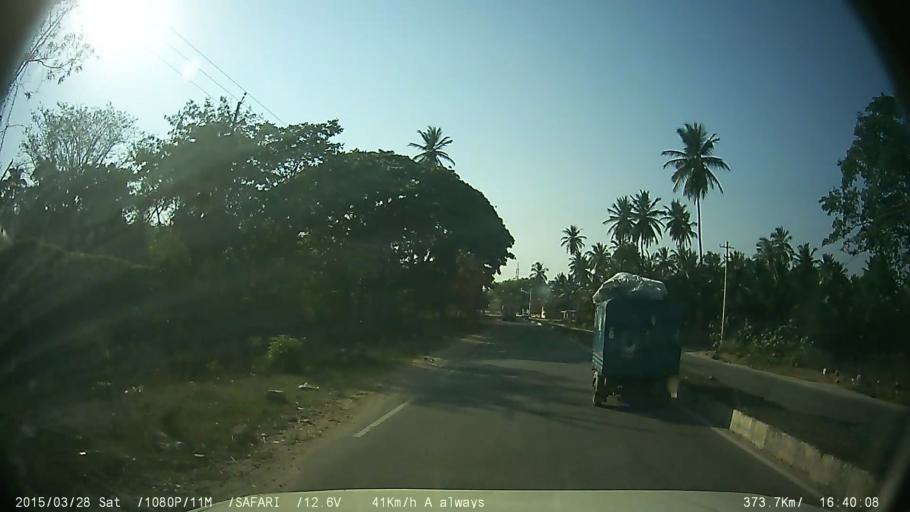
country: IN
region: Karnataka
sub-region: Mandya
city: Shrirangapattana
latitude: 12.3922
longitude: 76.5877
